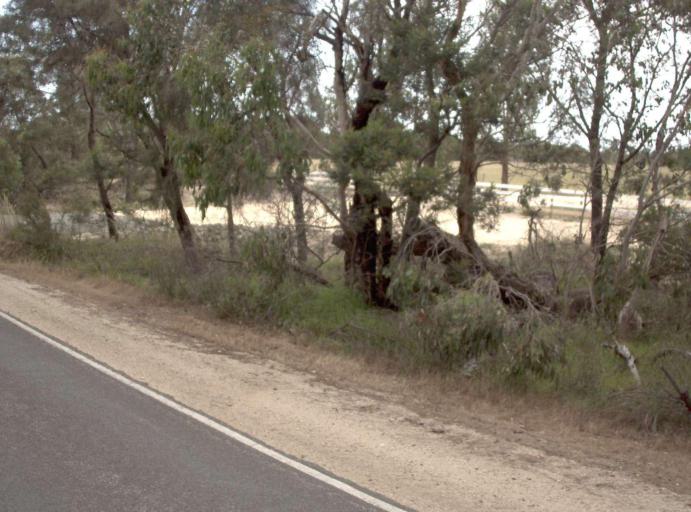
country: AU
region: Victoria
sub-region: Wellington
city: Sale
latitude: -38.1932
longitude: 147.0942
